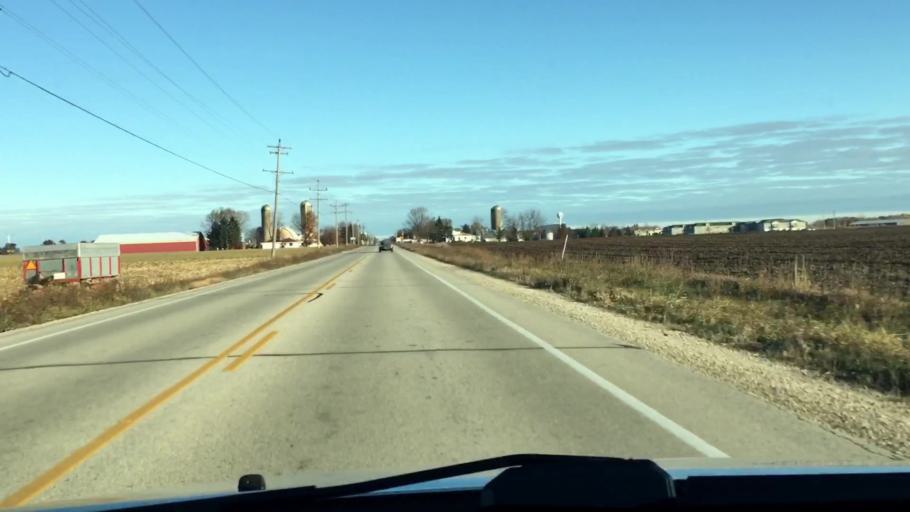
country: US
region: Wisconsin
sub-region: Dodge County
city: Lomira
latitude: 43.6113
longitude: -88.4504
